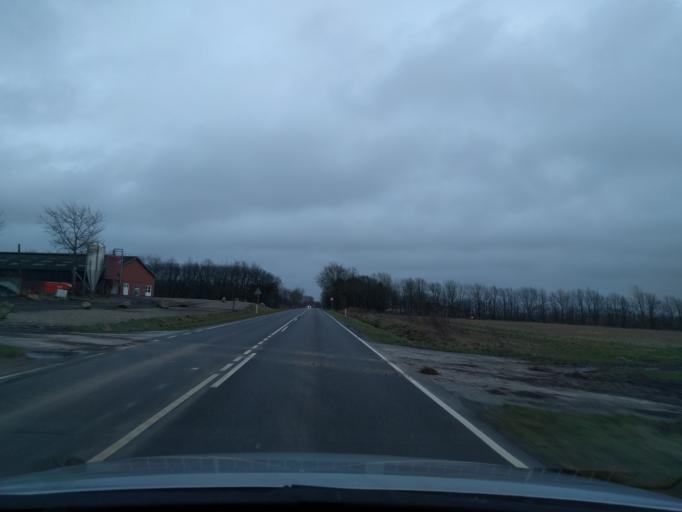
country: DK
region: South Denmark
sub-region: Haderslev Kommune
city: Vojens
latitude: 55.2433
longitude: 9.2117
